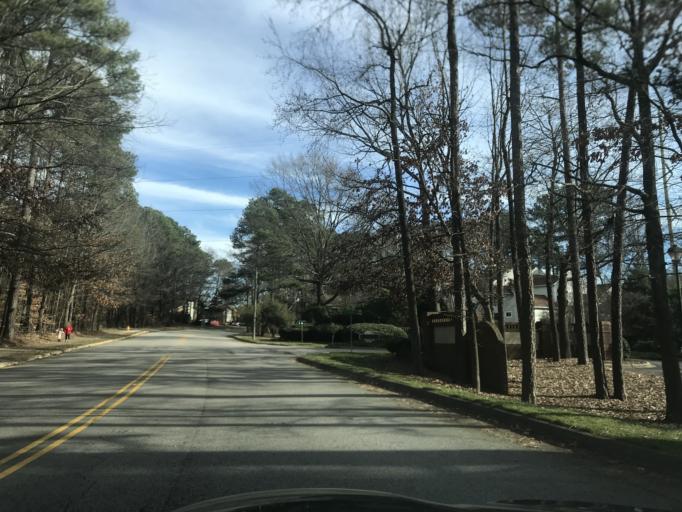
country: US
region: North Carolina
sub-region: Wake County
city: Cary
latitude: 35.7775
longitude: -78.7428
